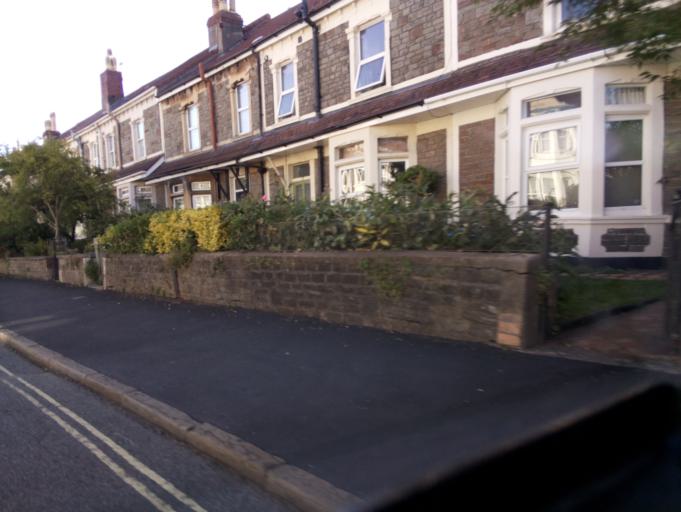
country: GB
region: England
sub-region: Bath and North East Somerset
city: Whitchurch
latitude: 51.4362
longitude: -2.5522
